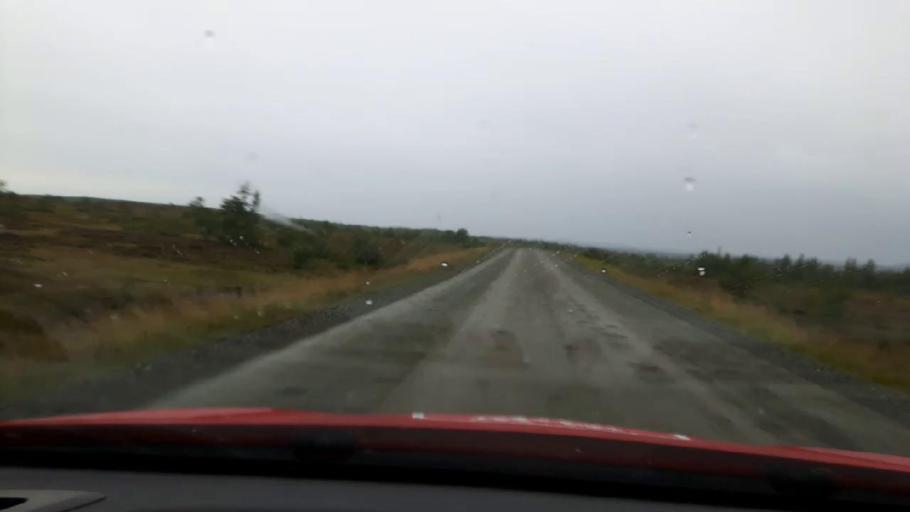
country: NO
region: Nord-Trondelag
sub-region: Meraker
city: Meraker
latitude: 63.6039
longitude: 12.2770
